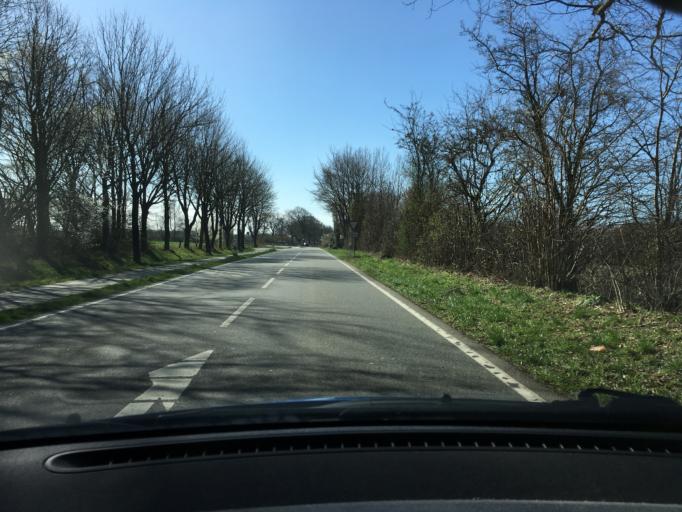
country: DE
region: Schleswig-Holstein
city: Kosel
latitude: 54.4932
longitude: 9.7476
